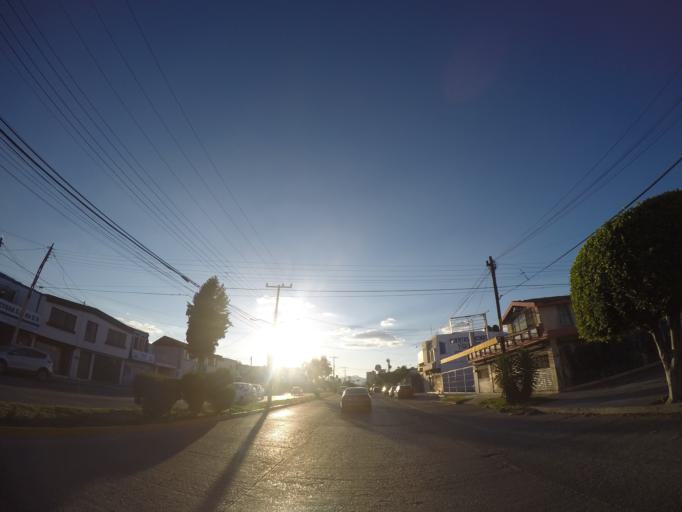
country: MX
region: San Luis Potosi
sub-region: San Luis Potosi
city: San Luis Potosi
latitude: 22.1346
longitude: -100.9780
